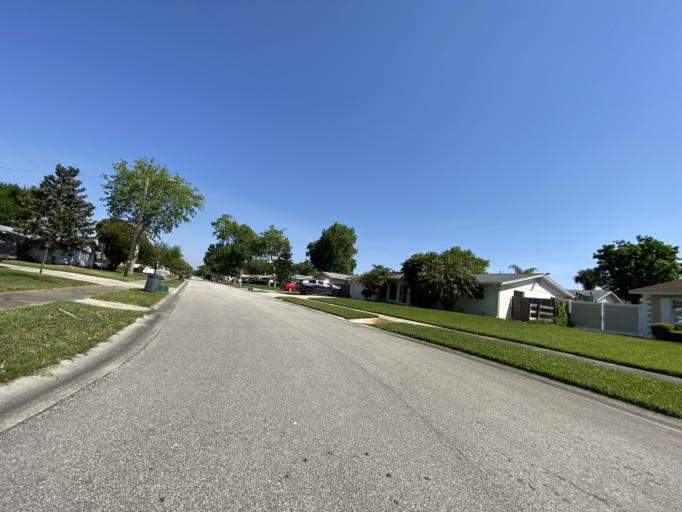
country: US
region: Florida
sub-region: Volusia County
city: South Daytona
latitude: 29.1613
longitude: -81.0084
